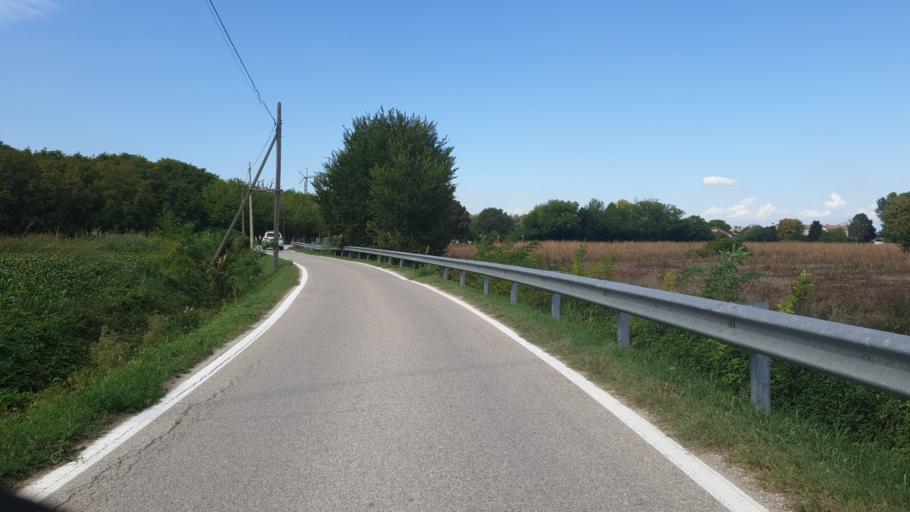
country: IT
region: Veneto
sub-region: Provincia di Padova
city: Terradura
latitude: 45.3333
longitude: 11.8153
